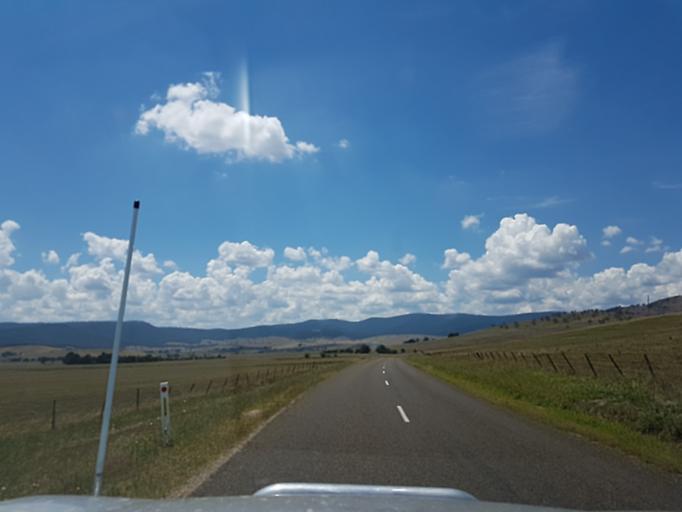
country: AU
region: Victoria
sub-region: Alpine
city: Mount Beauty
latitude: -36.9579
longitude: 147.7559
